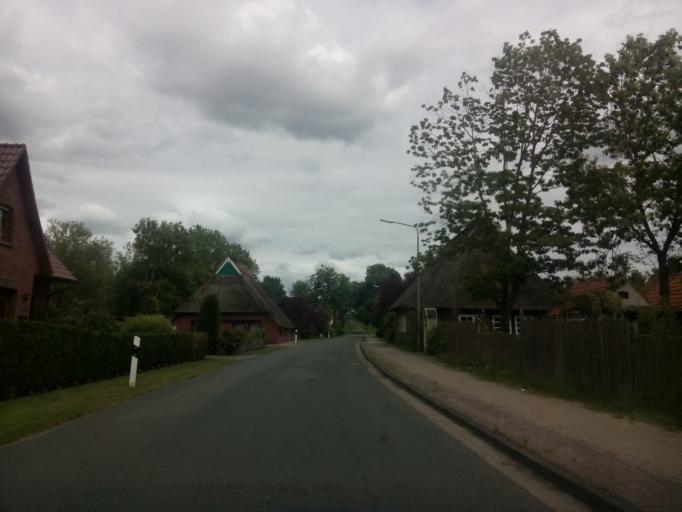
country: DE
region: Lower Saxony
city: Lemwerder
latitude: 53.1453
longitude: 8.6157
